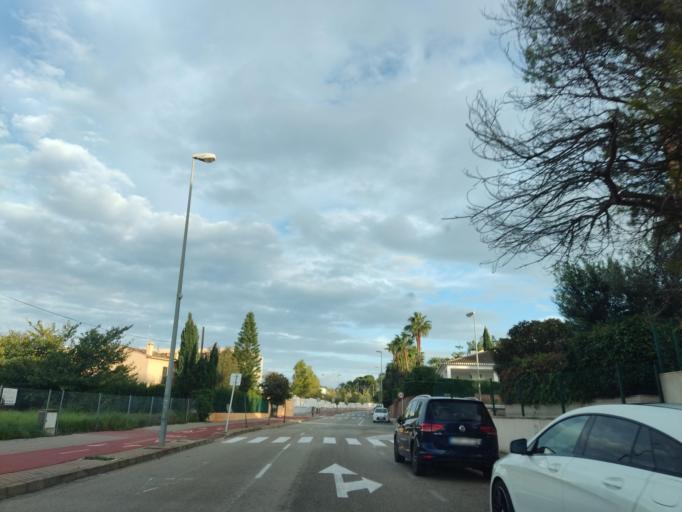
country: ES
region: Valencia
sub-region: Provincia de Alicante
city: Denia
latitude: 38.8329
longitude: 0.1128
